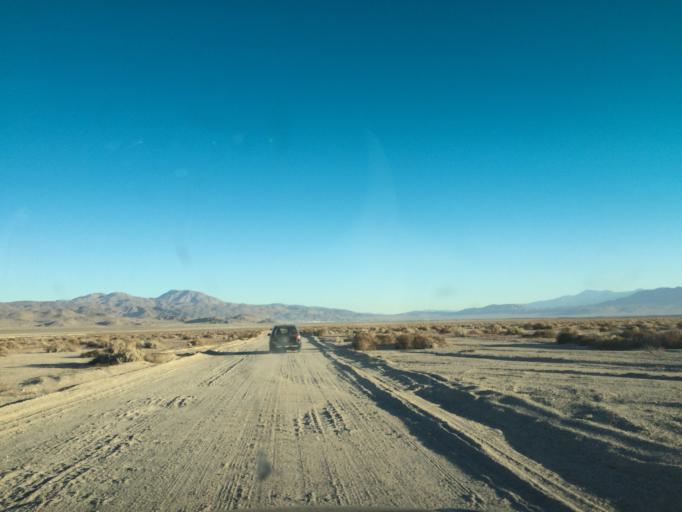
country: US
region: California
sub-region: San Bernardino County
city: Searles Valley
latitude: 35.6402
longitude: -117.3759
